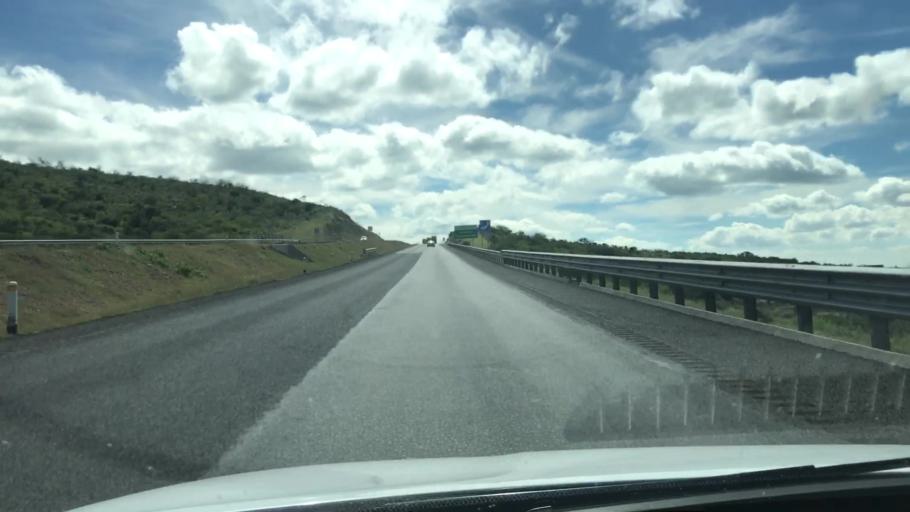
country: MX
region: Guanajuato
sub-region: Irapuato
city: Ex-Hacienda del Copal
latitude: 20.7396
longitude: -101.3079
